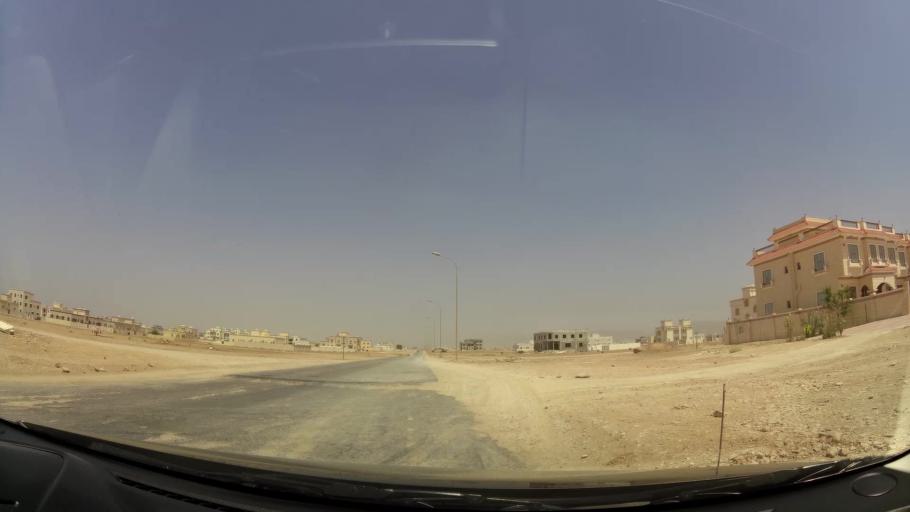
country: OM
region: Zufar
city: Salalah
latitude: 17.0920
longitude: 54.2157
